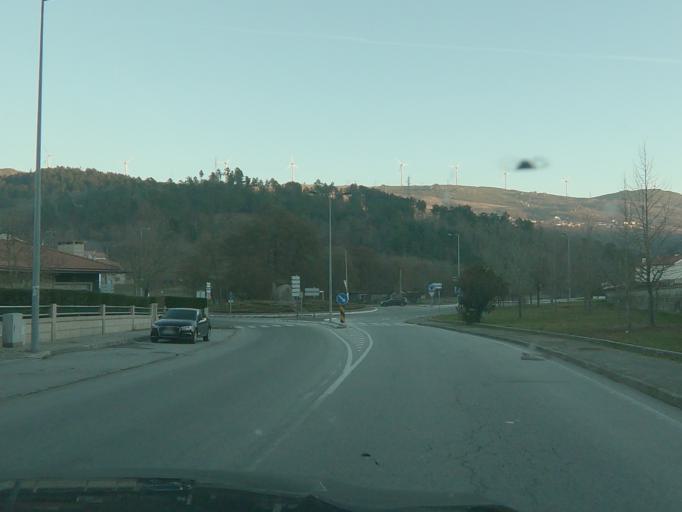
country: PT
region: Vila Real
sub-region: Vila Pouca de Aguiar
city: Vila Pouca de Aguiar
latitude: 41.4906
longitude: -7.6497
